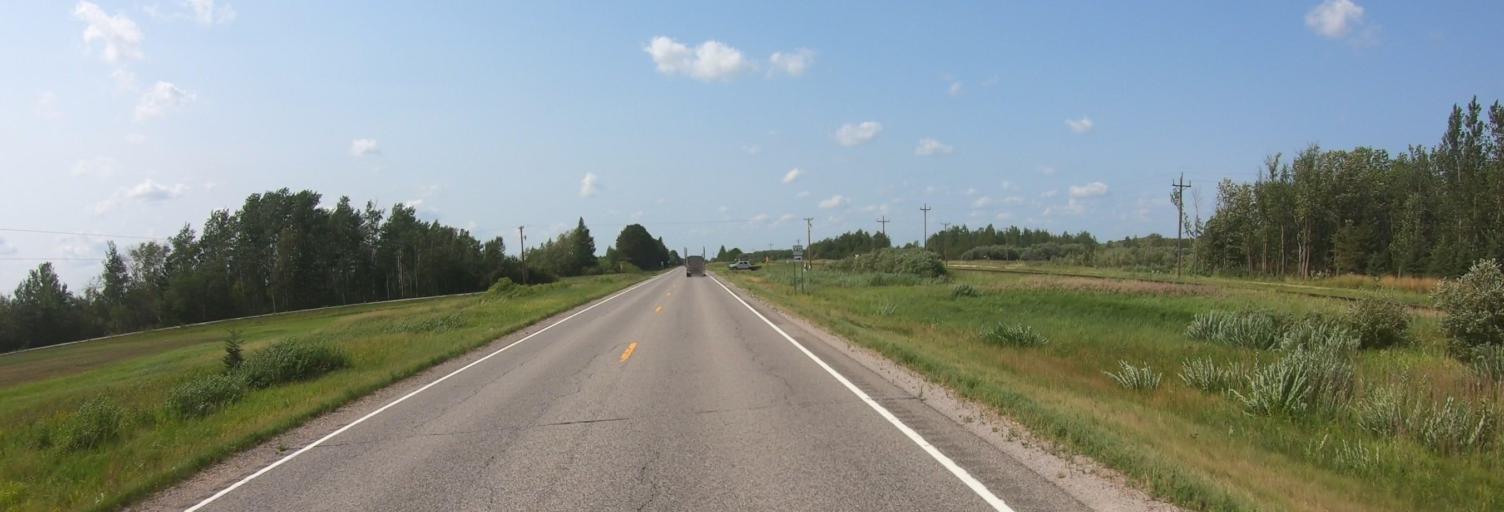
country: US
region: Minnesota
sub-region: Roseau County
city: Warroad
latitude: 48.8257
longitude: -95.1546
